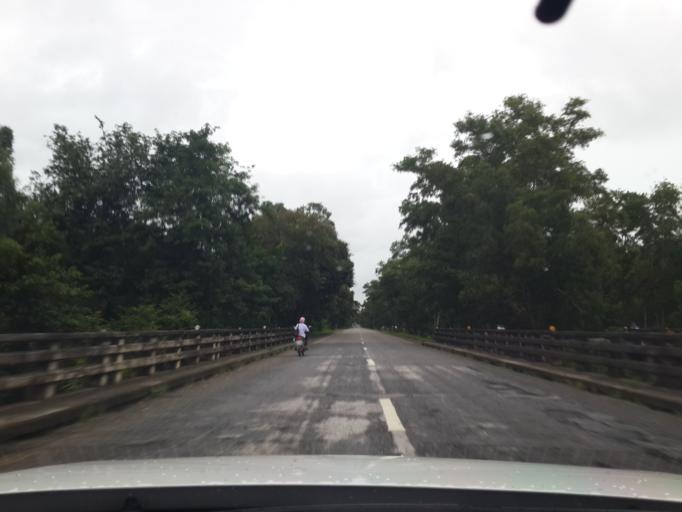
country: TH
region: Songkhla
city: Na Mom
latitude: 6.9640
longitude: 100.5691
